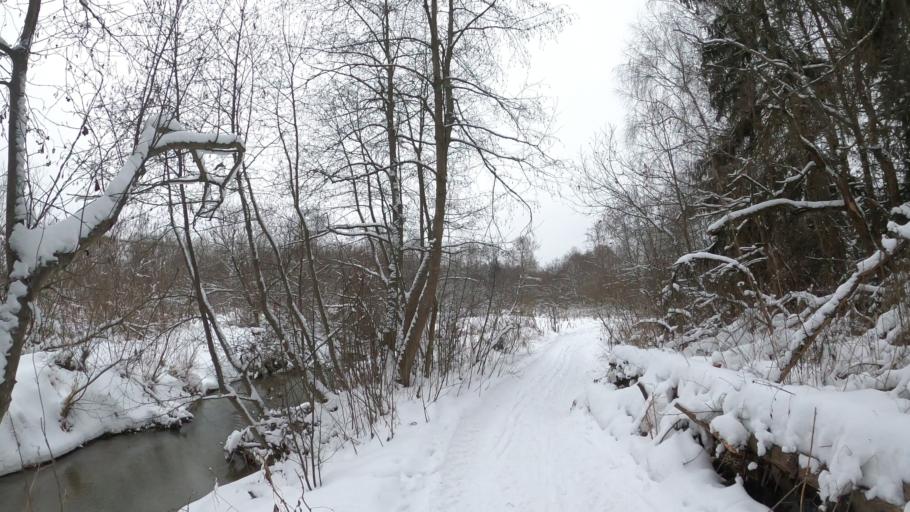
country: RU
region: Moskovskaya
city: Firsanovka
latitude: 55.9391
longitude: 37.2223
